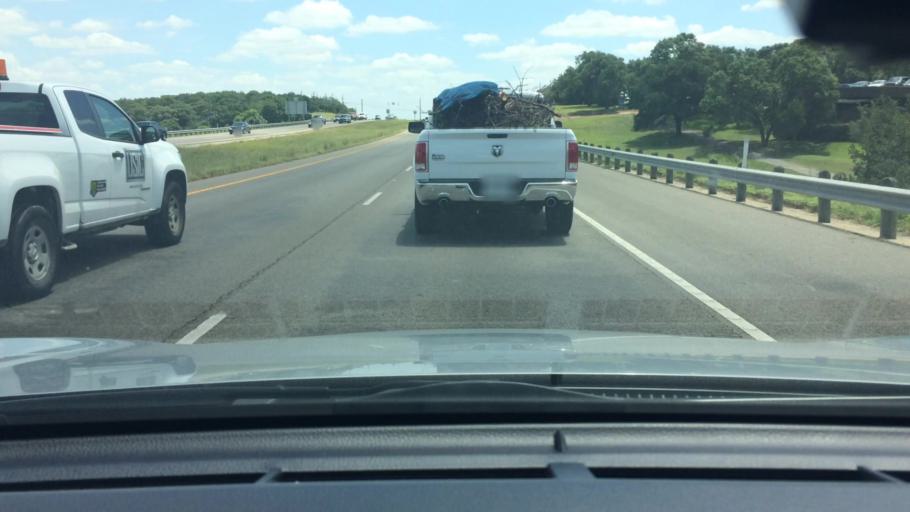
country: US
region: Texas
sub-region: Travis County
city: Lost Creek
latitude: 30.2822
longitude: -97.8232
